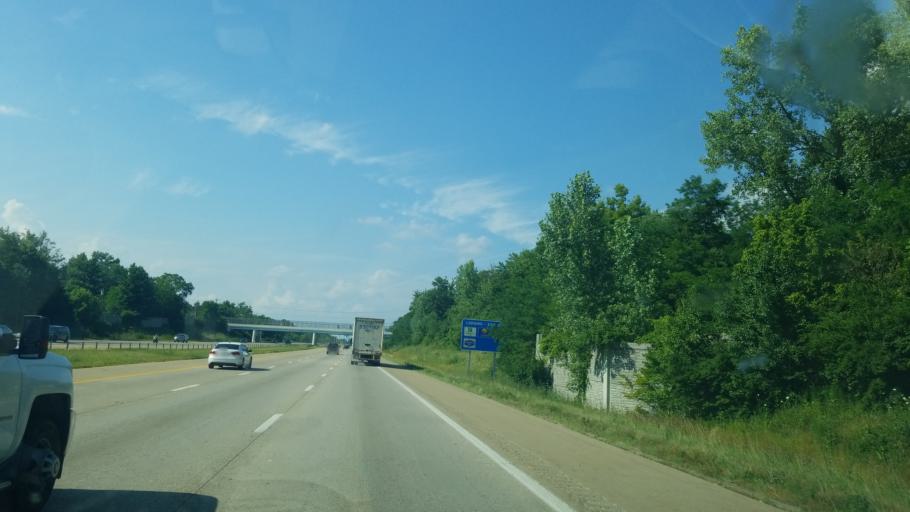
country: US
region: Ohio
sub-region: Clermont County
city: Withamsville
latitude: 39.0821
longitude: -84.2901
